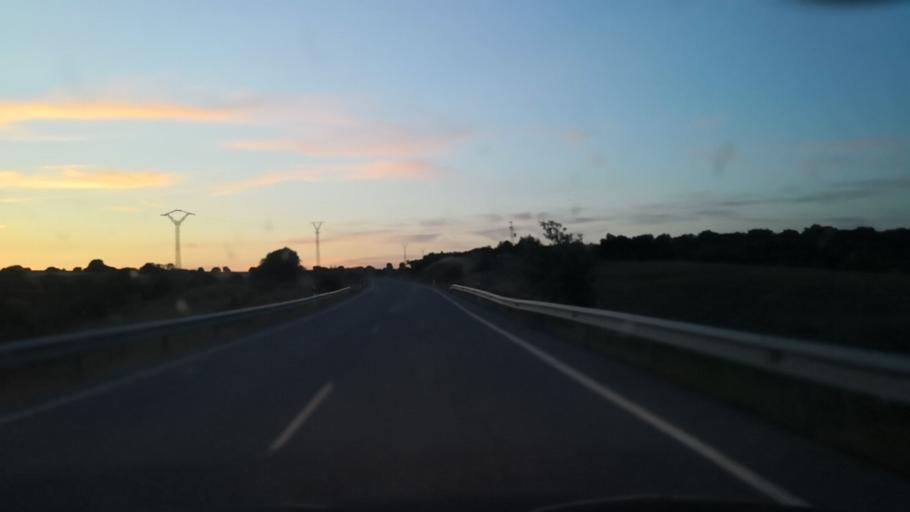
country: ES
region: Extremadura
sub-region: Provincia de Caceres
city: Piedras Albas
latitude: 39.7689
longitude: -6.9133
